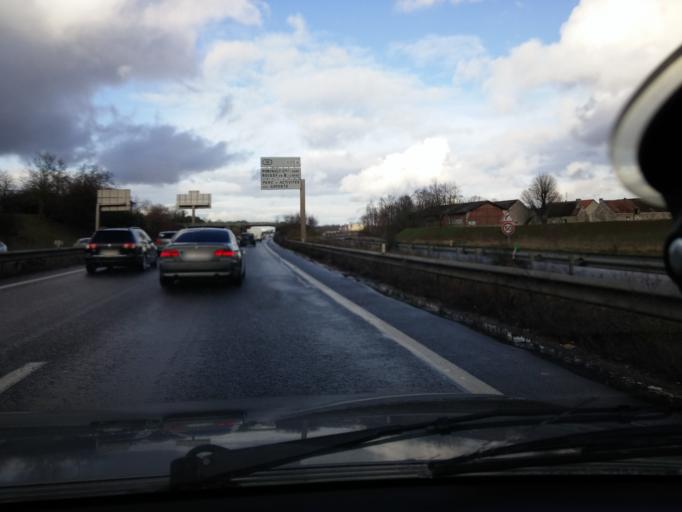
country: FR
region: Ile-de-France
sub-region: Departement de Seine-et-Marne
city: Pontault-Combault
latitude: 48.7936
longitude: 2.6200
